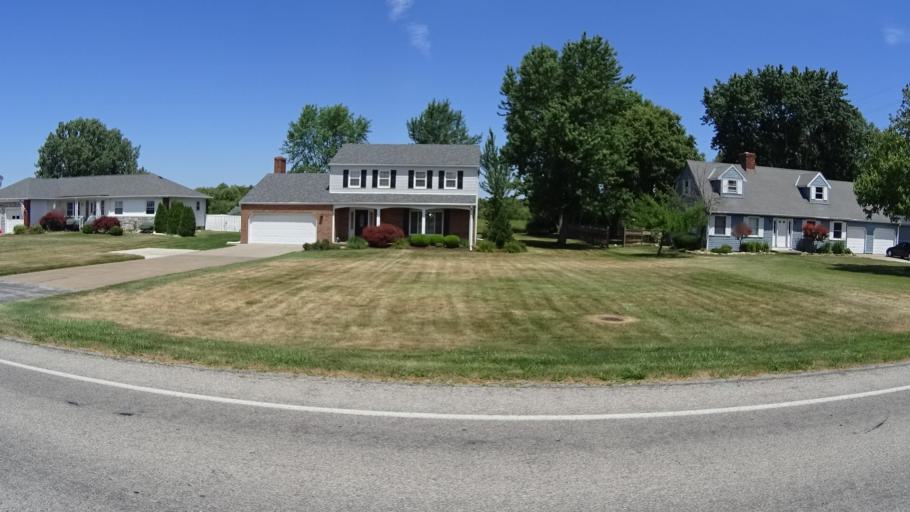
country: US
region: Ohio
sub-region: Erie County
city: Sandusky
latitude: 41.3964
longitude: -82.6941
